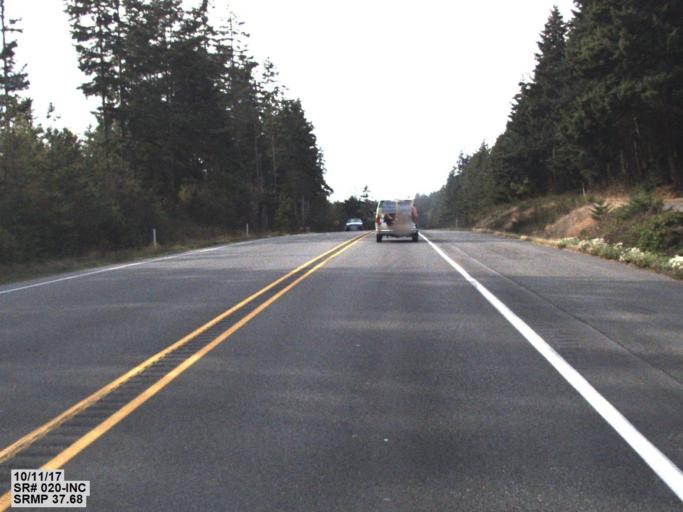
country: US
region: Washington
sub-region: Island County
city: Ault Field
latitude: 48.3582
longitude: -122.6269
